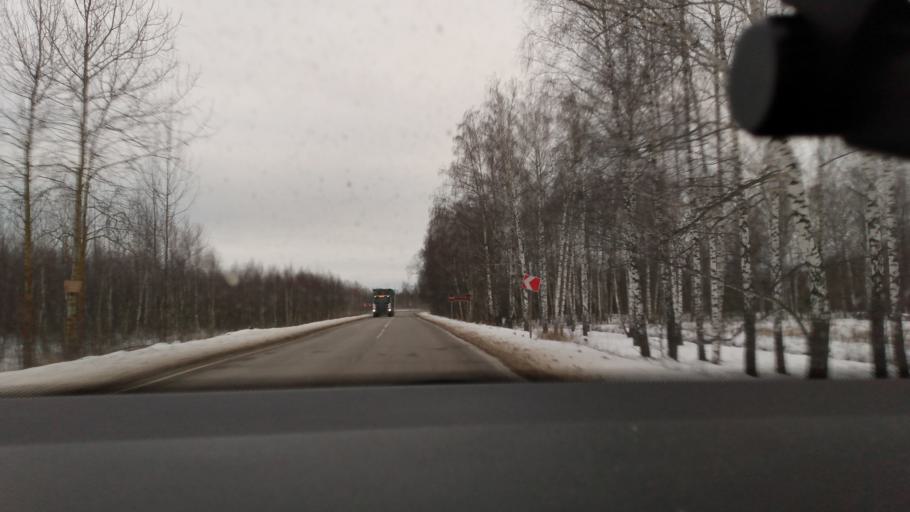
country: RU
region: Moskovskaya
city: Krasnaya Poyma
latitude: 55.1391
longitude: 39.2081
